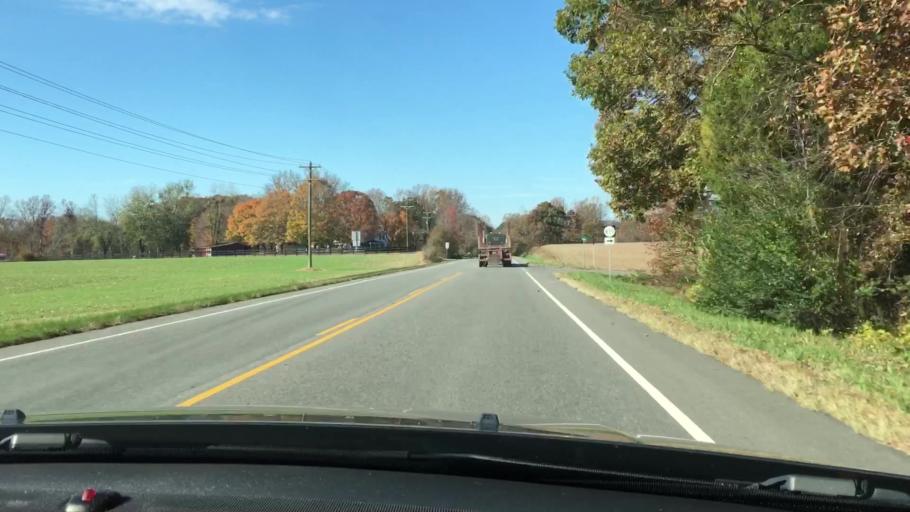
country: US
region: Virginia
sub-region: Hanover County
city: Hanover
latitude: 37.8035
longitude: -77.2639
